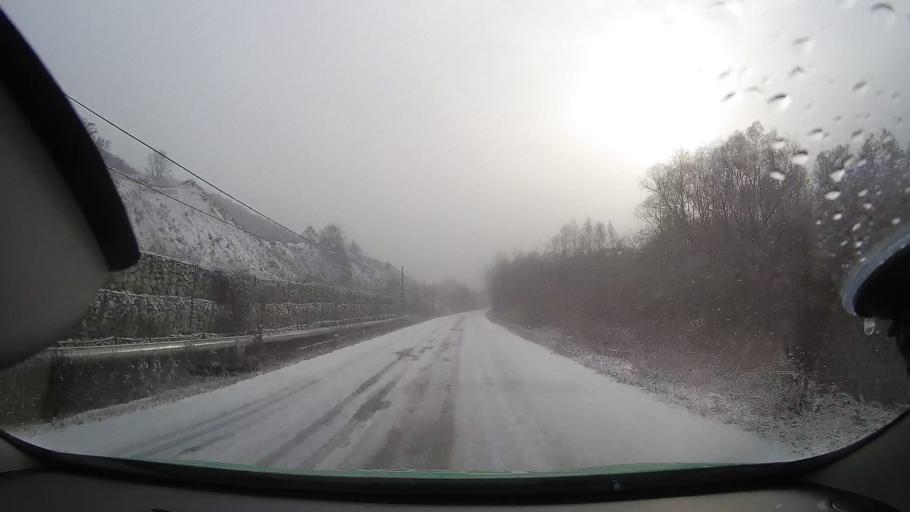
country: RO
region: Alba
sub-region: Comuna Livezile
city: Livezile
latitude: 46.3591
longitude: 23.6128
